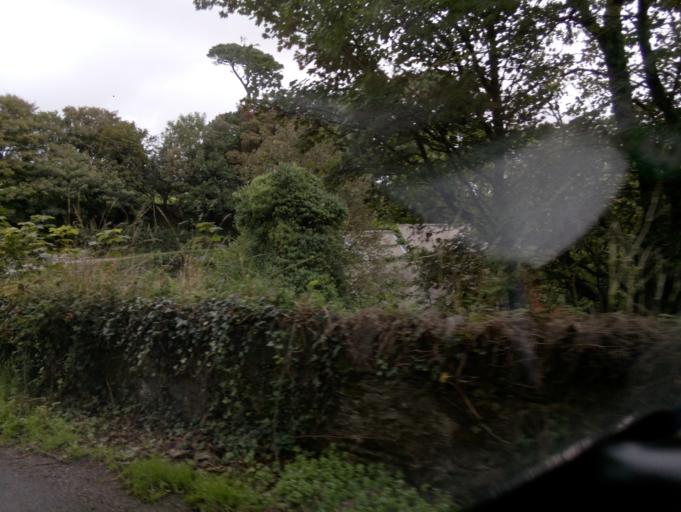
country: GB
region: England
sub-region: Devon
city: Dartmouth
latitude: 50.3147
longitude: -3.6257
